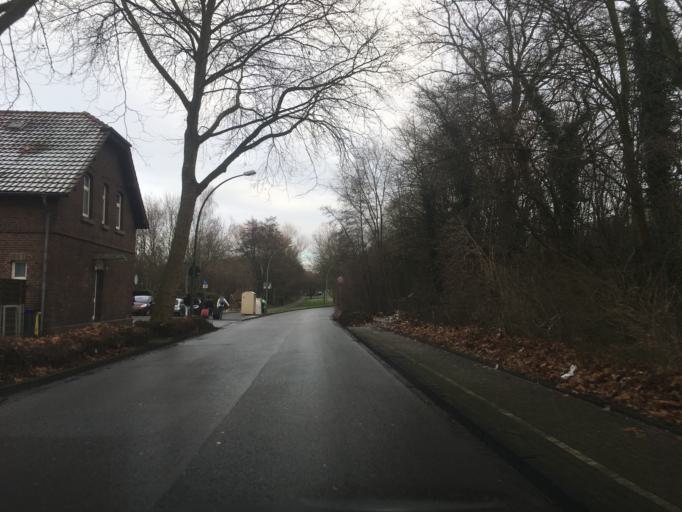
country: DE
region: North Rhine-Westphalia
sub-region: Regierungsbezirk Munster
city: Bottrop
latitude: 51.5169
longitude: 6.9461
